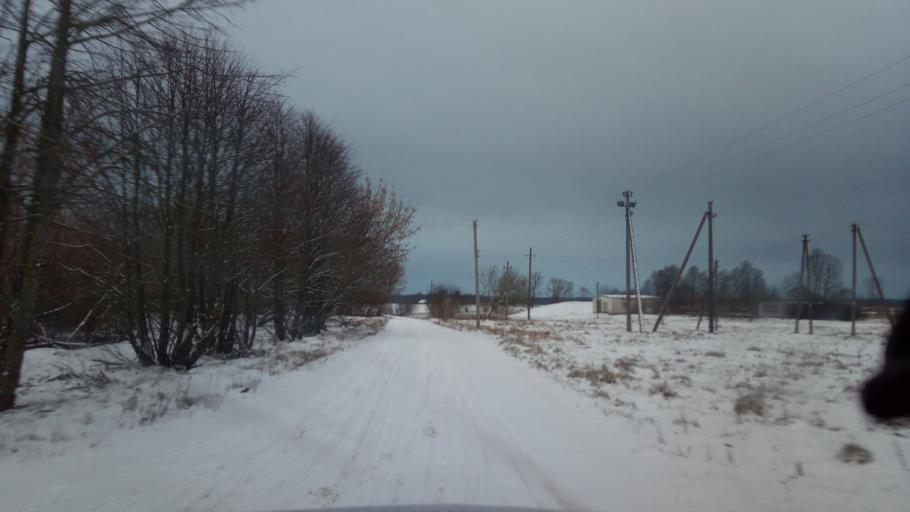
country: LT
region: Vilnius County
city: Ukmerge
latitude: 55.4795
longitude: 24.6186
